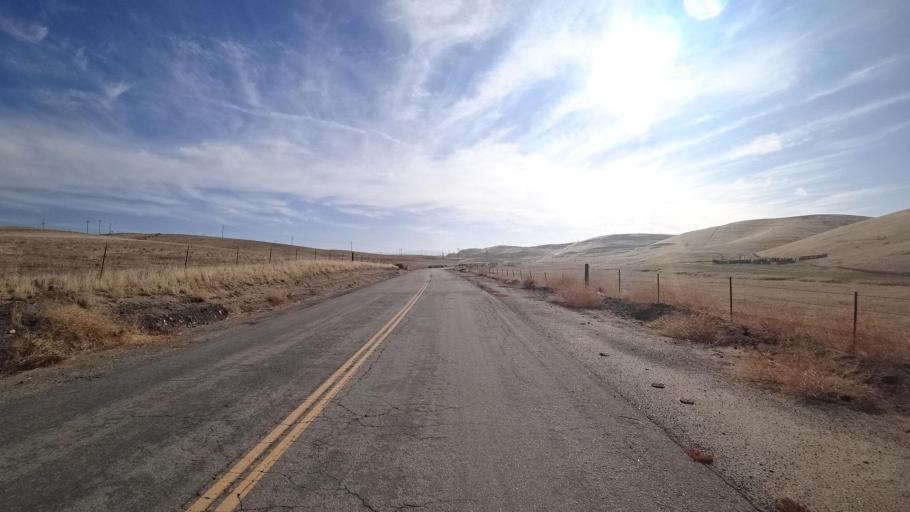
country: US
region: California
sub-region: Kern County
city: Oildale
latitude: 35.6157
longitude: -118.9844
